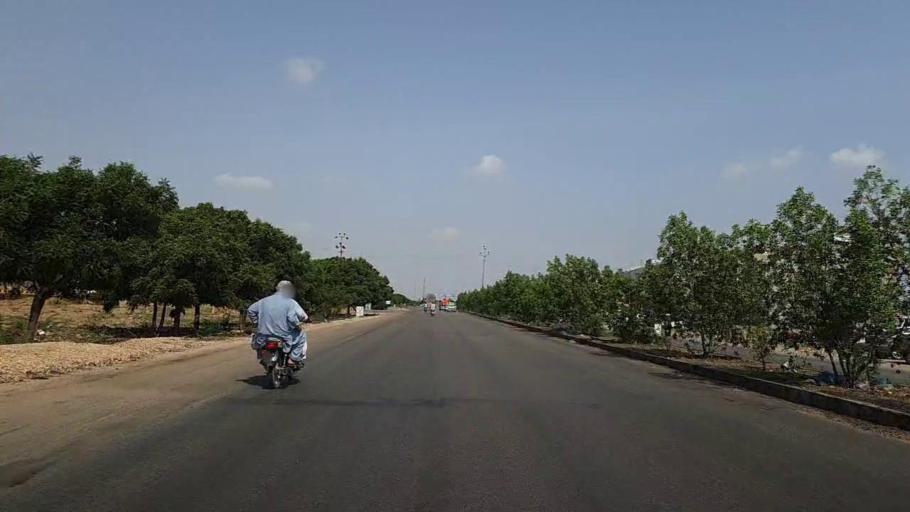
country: PK
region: Sindh
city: Gharo
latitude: 24.8562
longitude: 67.4093
